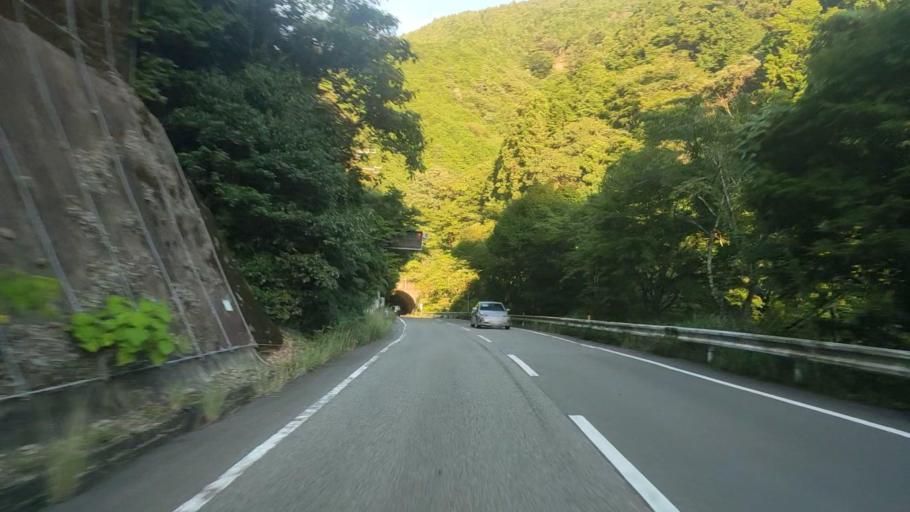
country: JP
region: Wakayama
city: Tanabe
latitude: 33.8148
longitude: 135.5769
